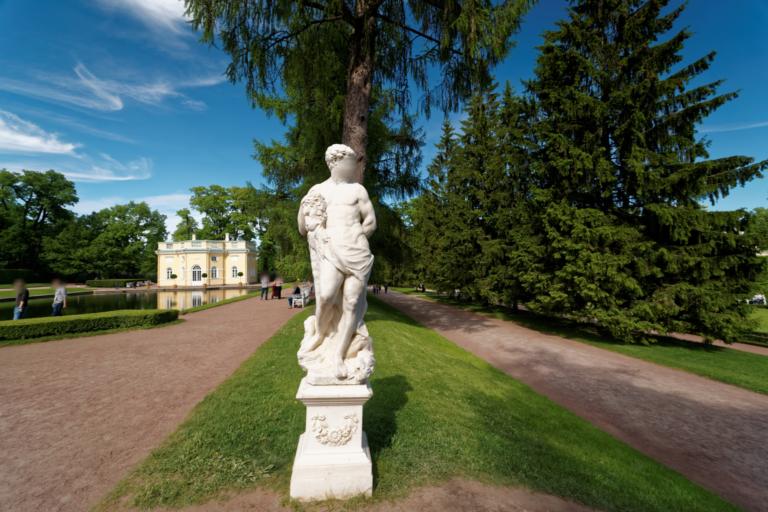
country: RU
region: St.-Petersburg
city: Pushkin
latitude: 59.7152
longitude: 30.3980
